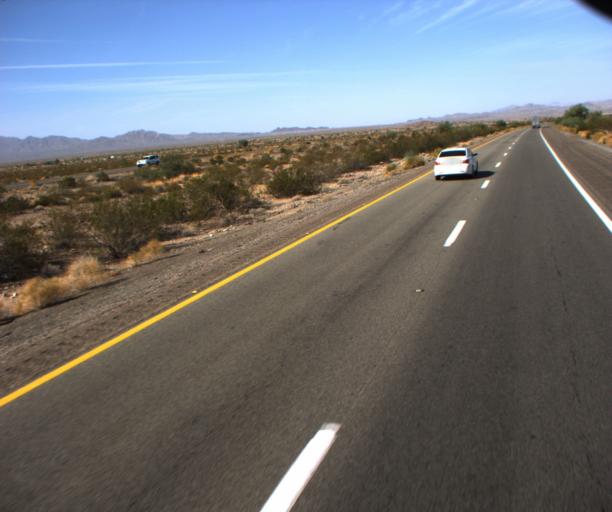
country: US
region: Arizona
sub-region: Mohave County
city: Desert Hills
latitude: 34.7546
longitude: -114.2175
